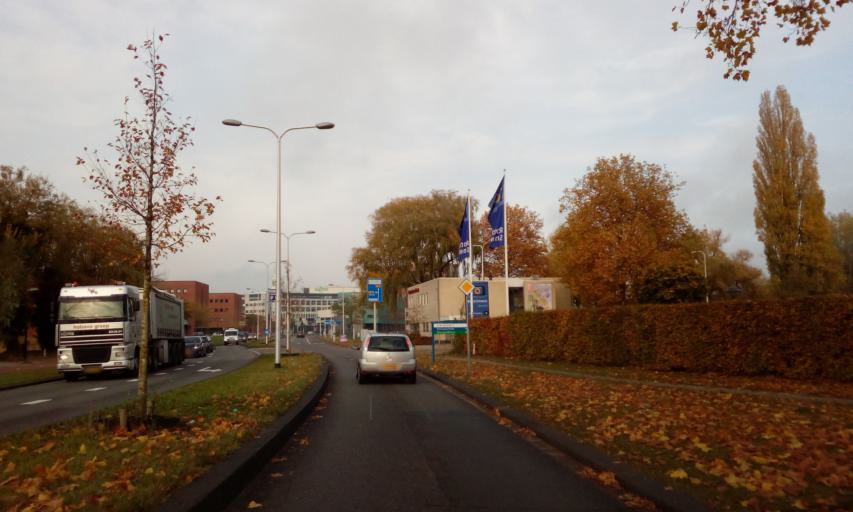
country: NL
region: Overijssel
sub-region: Gemeente Deventer
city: Deventer
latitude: 52.2502
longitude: 6.1691
